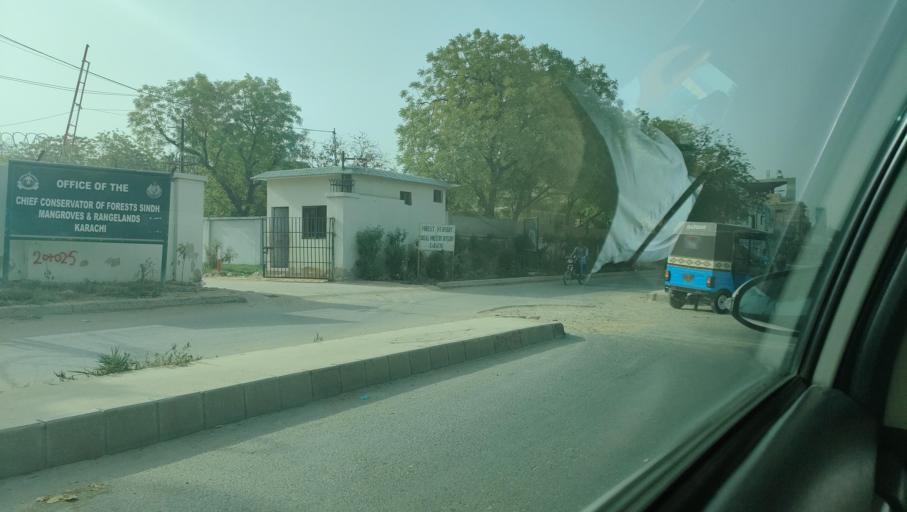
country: PK
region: Sindh
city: Malir Cantonment
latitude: 24.9067
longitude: 67.1831
